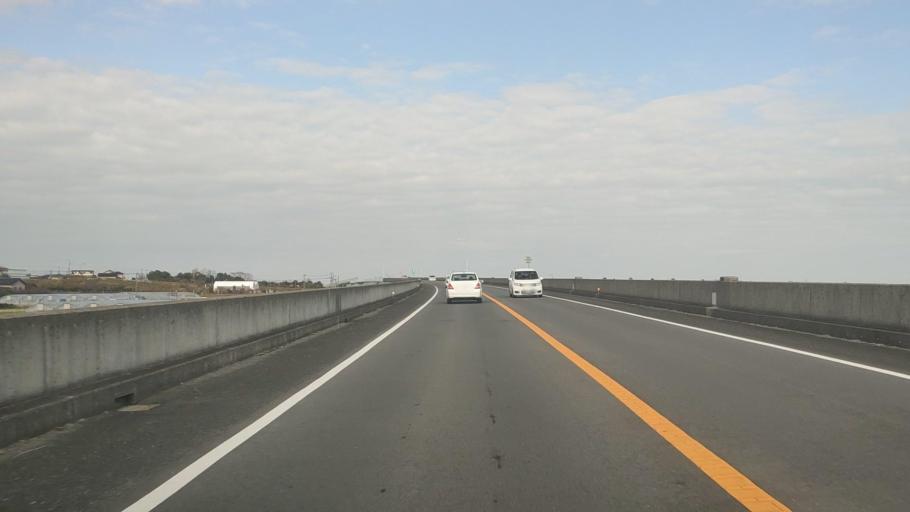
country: JP
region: Nagasaki
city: Shimabara
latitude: 32.7356
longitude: 130.3696
